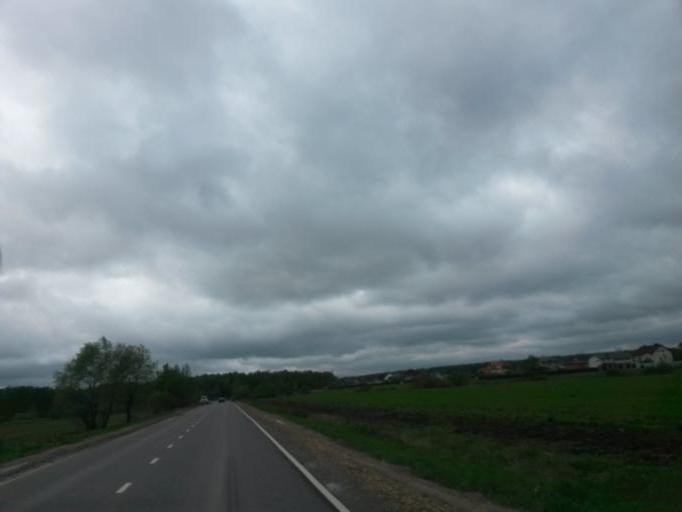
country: RU
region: Moskovskaya
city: Klimovsk
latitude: 55.3458
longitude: 37.5755
